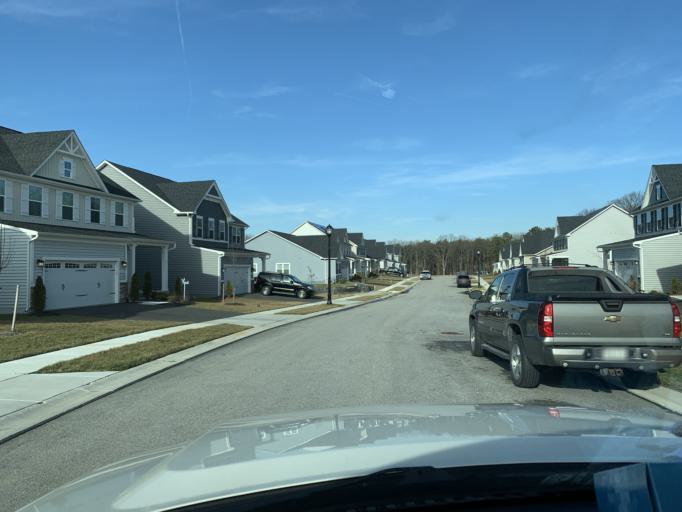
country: US
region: Maryland
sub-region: Anne Arundel County
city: Fort Meade
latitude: 39.1381
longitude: -76.7397
